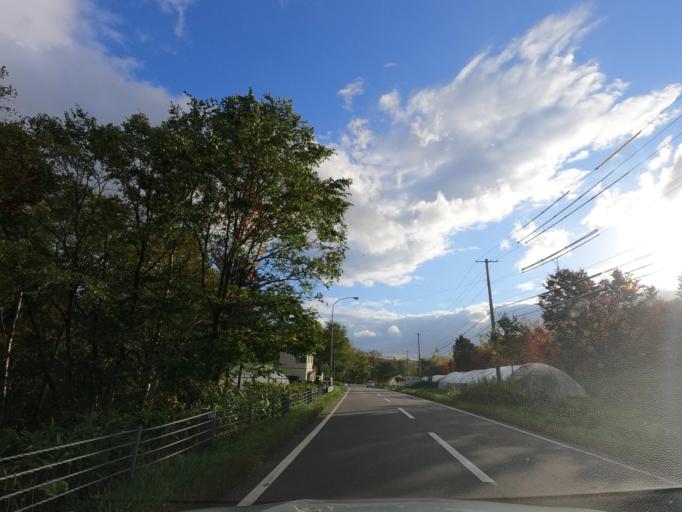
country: JP
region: Hokkaido
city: Date
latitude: 42.6522
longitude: 141.0635
